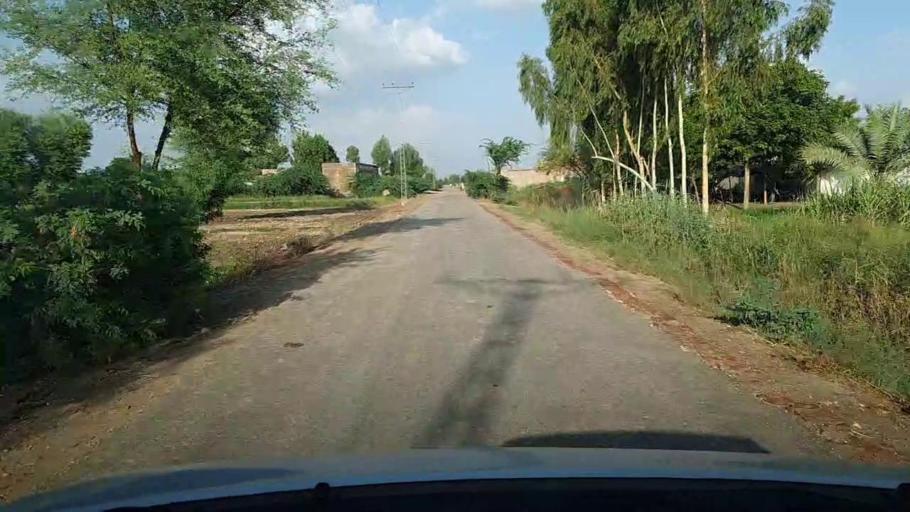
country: PK
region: Sindh
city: Hingorja
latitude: 27.0883
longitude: 68.4076
